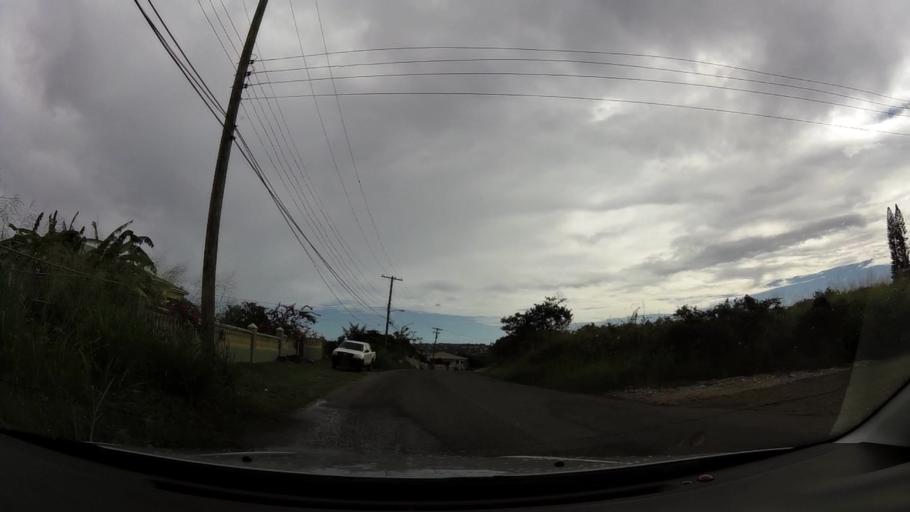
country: AG
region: Saint John
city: Potters Village
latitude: 17.0908
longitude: -61.8133
